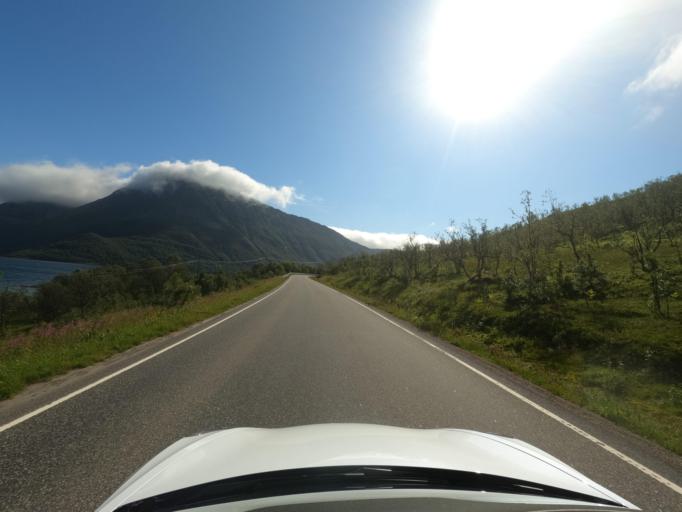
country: NO
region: Nordland
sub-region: Lodingen
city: Lodingen
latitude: 68.6140
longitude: 15.7682
